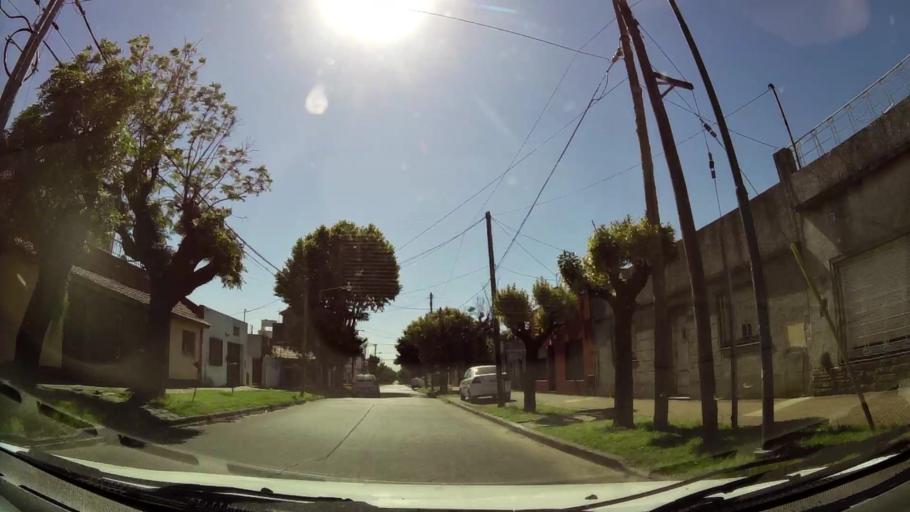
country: AR
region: Buenos Aires
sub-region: Partido de General San Martin
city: General San Martin
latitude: -34.5412
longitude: -58.5750
